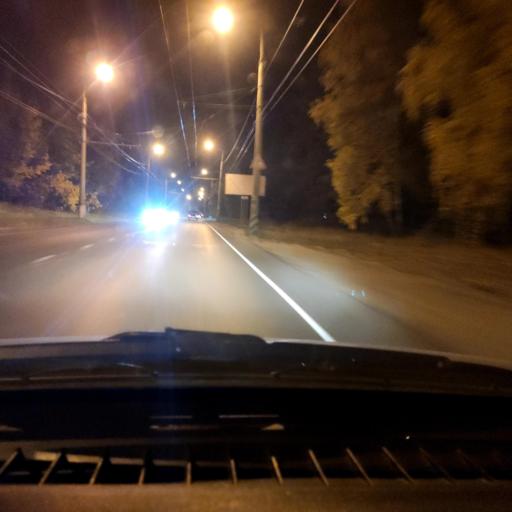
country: RU
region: Samara
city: Tol'yatti
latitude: 53.4929
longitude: 49.3859
